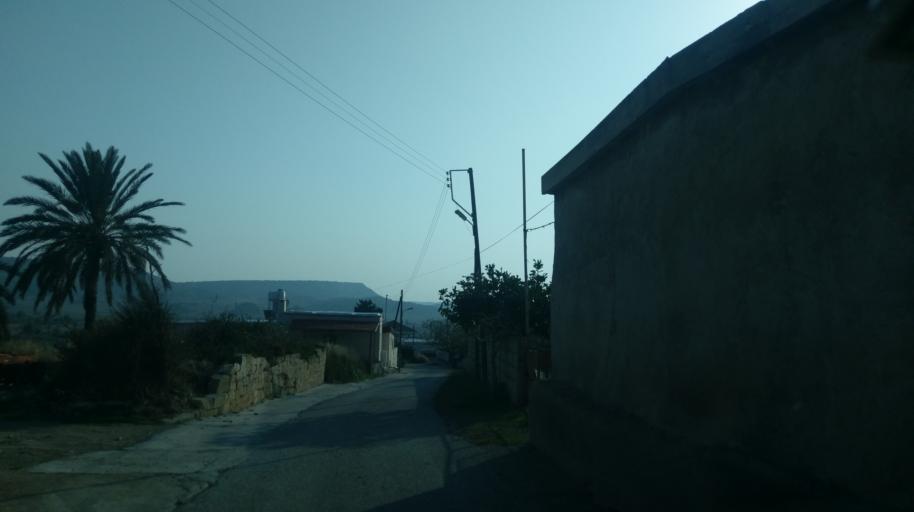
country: CY
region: Ammochostos
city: Leonarisso
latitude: 35.4787
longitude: 34.1064
